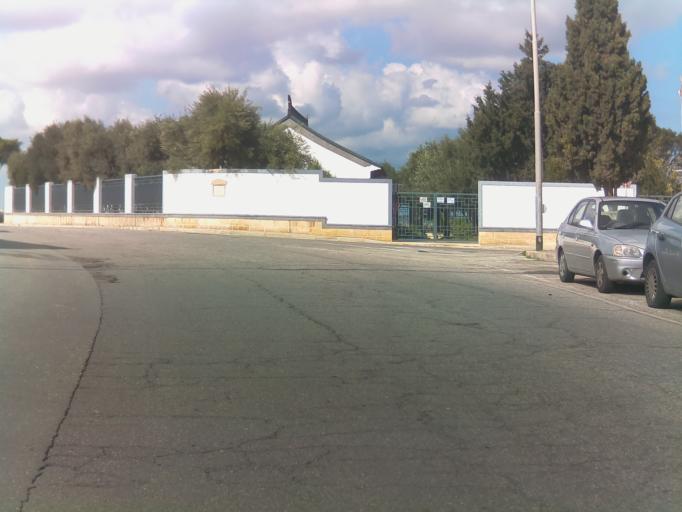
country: MT
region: Saint Lucia
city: Santa Lucija
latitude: 35.8628
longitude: 14.5017
